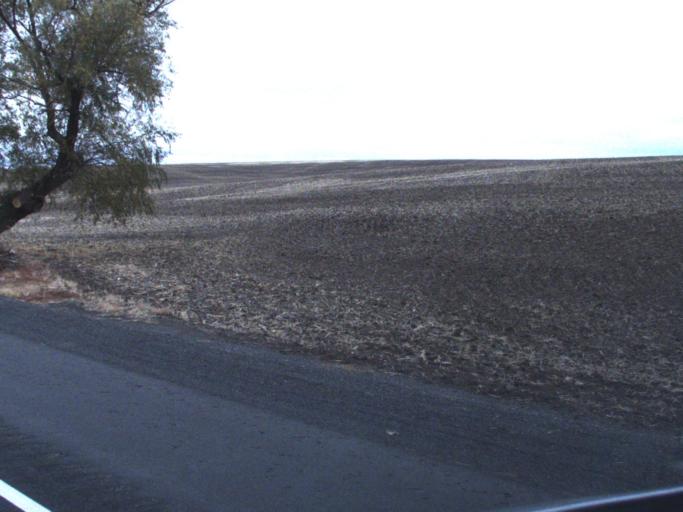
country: US
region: Washington
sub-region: Asotin County
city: Clarkston
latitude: 46.5031
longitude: -117.0785
